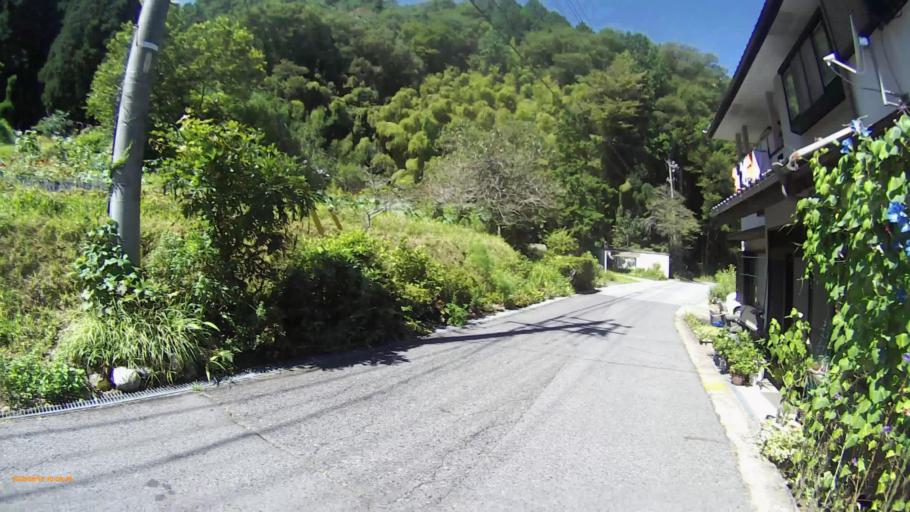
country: JP
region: Nagano
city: Iida
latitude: 35.6837
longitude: 137.6631
